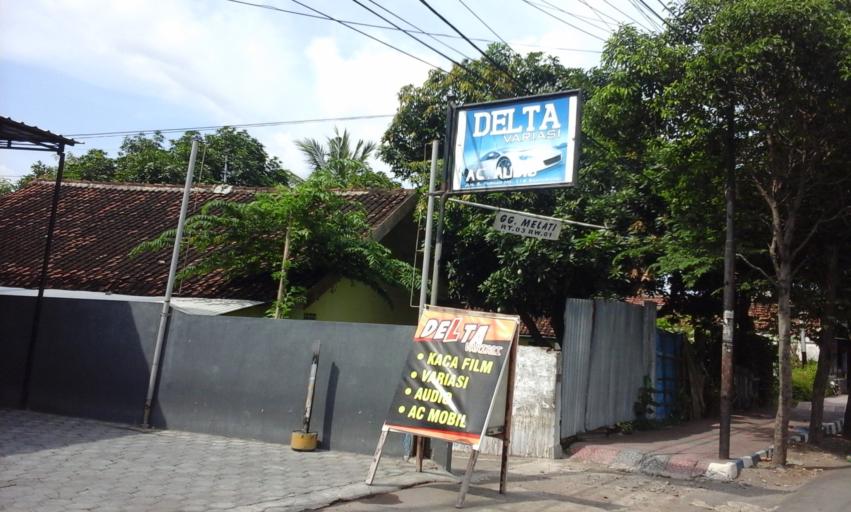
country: ID
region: East Java
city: Krajan
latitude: -8.2437
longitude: 114.3522
